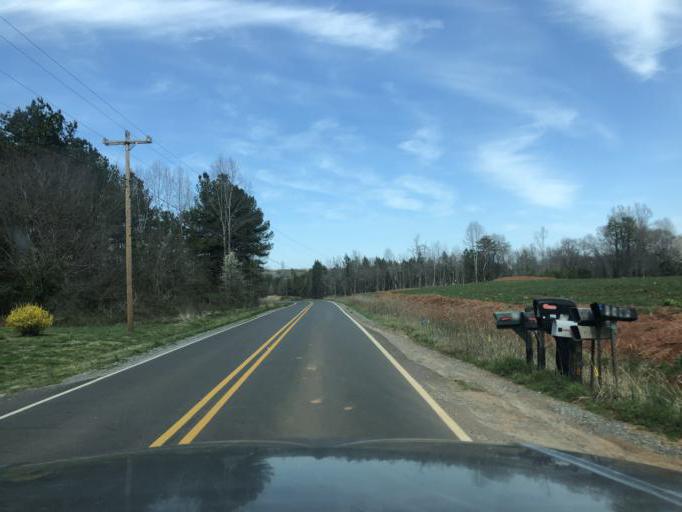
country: US
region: North Carolina
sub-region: Cleveland County
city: Shelby
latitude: 35.2476
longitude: -81.5409
